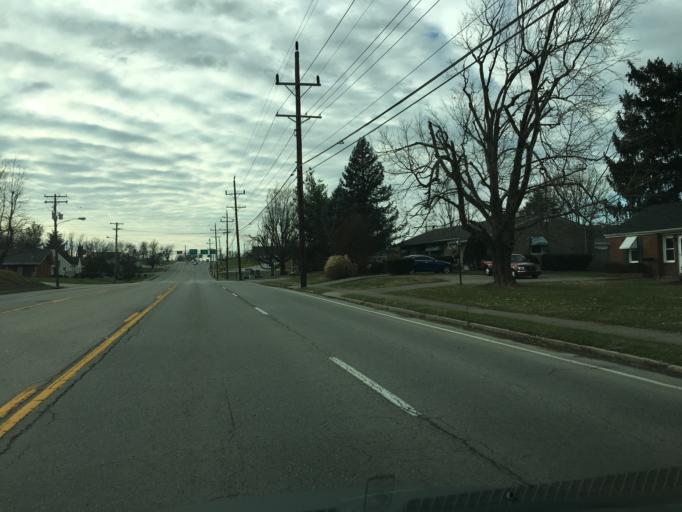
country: US
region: Kentucky
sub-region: Franklin County
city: Frankfort
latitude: 38.2077
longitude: -84.8309
